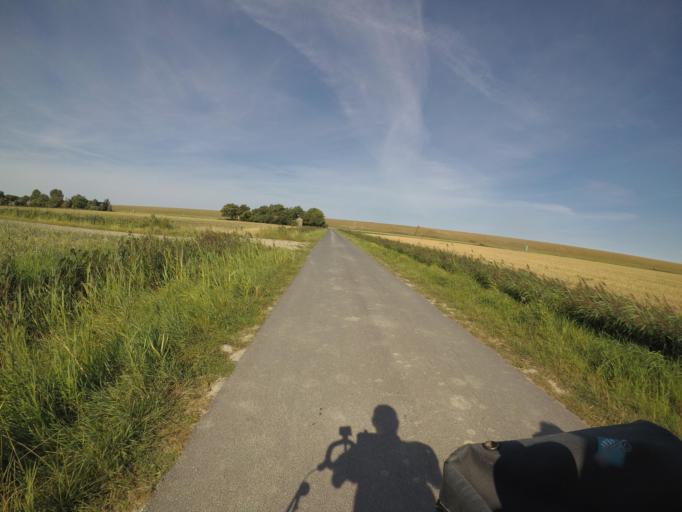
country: NL
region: Friesland
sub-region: Gemeente Ferwerderadiel
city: Marrum
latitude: 53.3419
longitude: 5.7986
